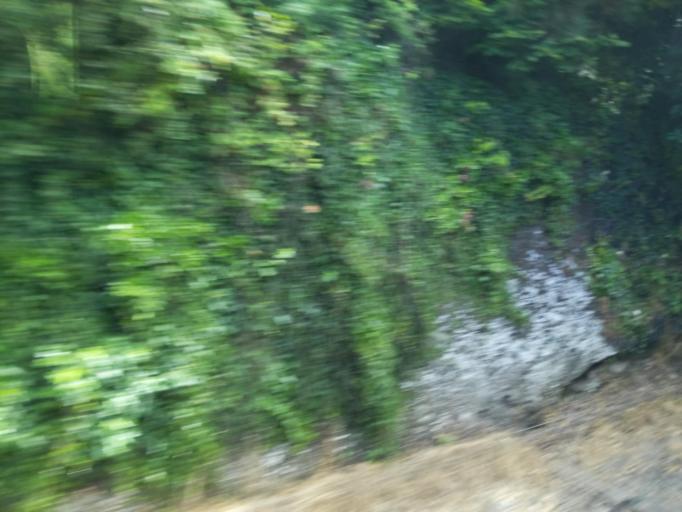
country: GB
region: England
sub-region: Cornwall
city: Par
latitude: 50.3572
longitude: -4.7043
